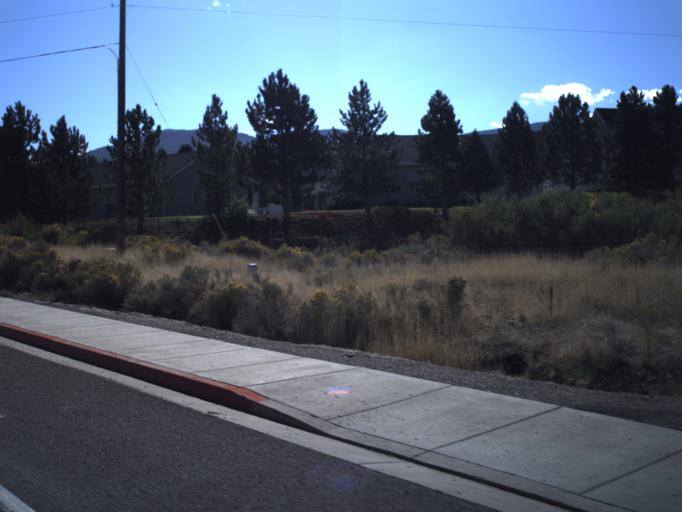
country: US
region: Utah
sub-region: Iron County
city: Cedar City
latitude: 37.6848
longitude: -113.0981
